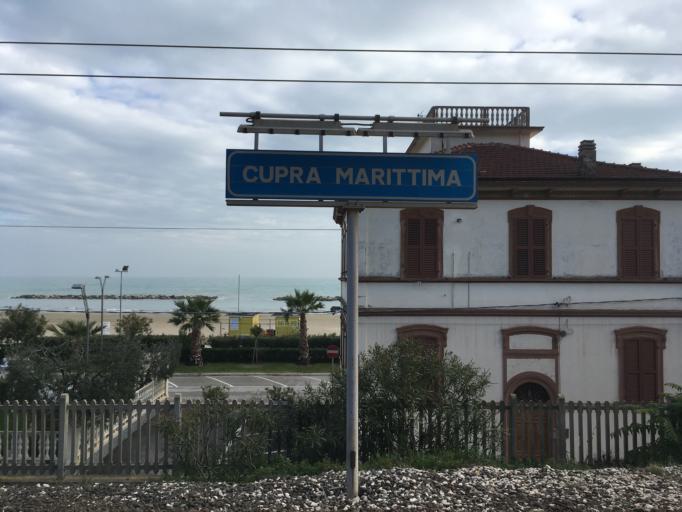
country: IT
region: The Marches
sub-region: Provincia di Ascoli Piceno
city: Cupra Marittima
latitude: 43.0235
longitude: 13.8608
